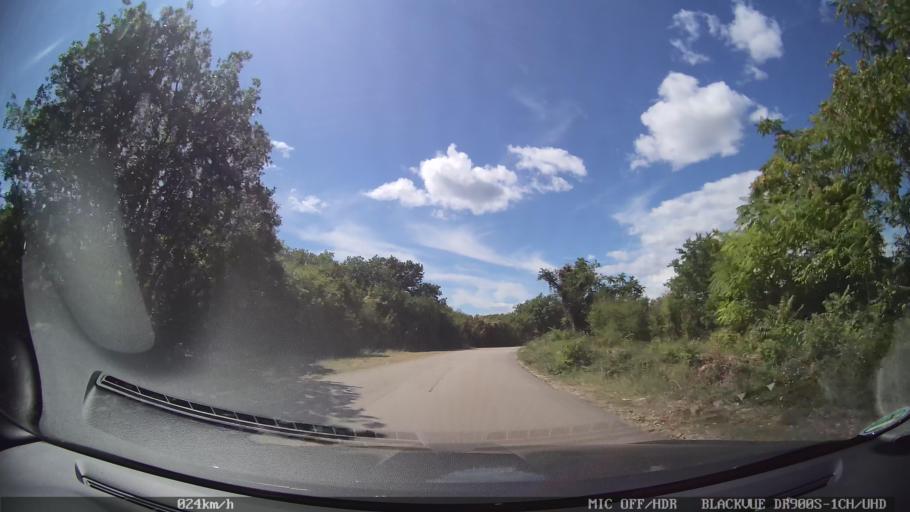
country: HR
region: Primorsko-Goranska
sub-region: Grad Krk
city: Krk
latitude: 45.0511
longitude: 14.5009
